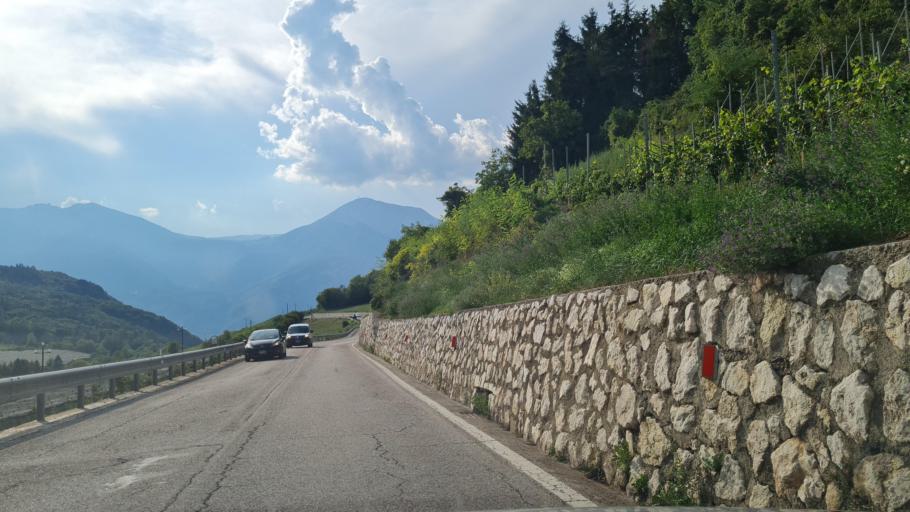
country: IT
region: Trentino-Alto Adige
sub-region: Provincia di Trento
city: Vigolo Vattaro
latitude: 46.0052
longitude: 11.1791
